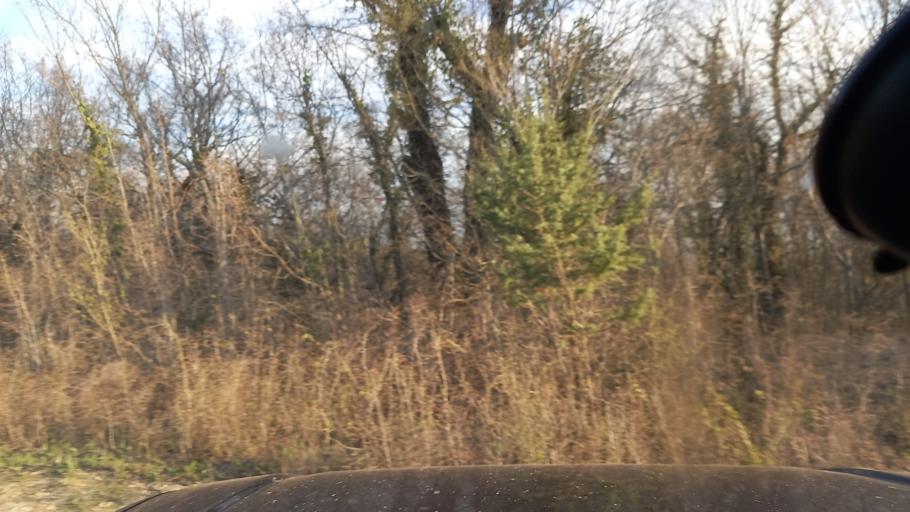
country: RU
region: Krasnodarskiy
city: Arkhipo-Osipovka
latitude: 44.3592
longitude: 38.5676
